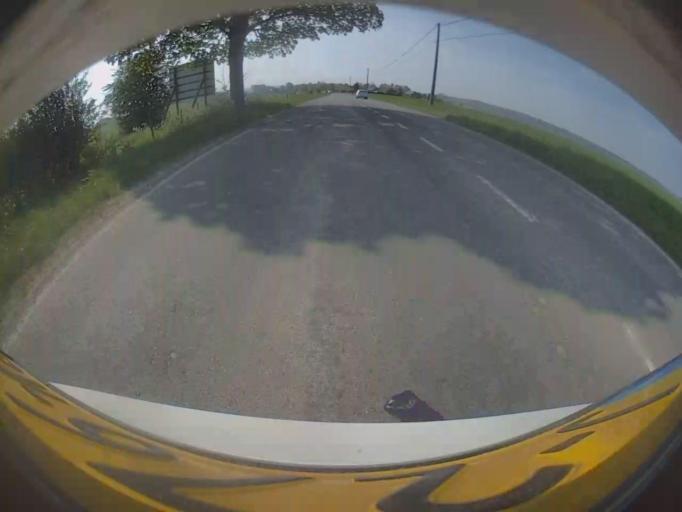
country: BE
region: Wallonia
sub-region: Province de Namur
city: Dinant
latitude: 50.2633
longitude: 4.9606
